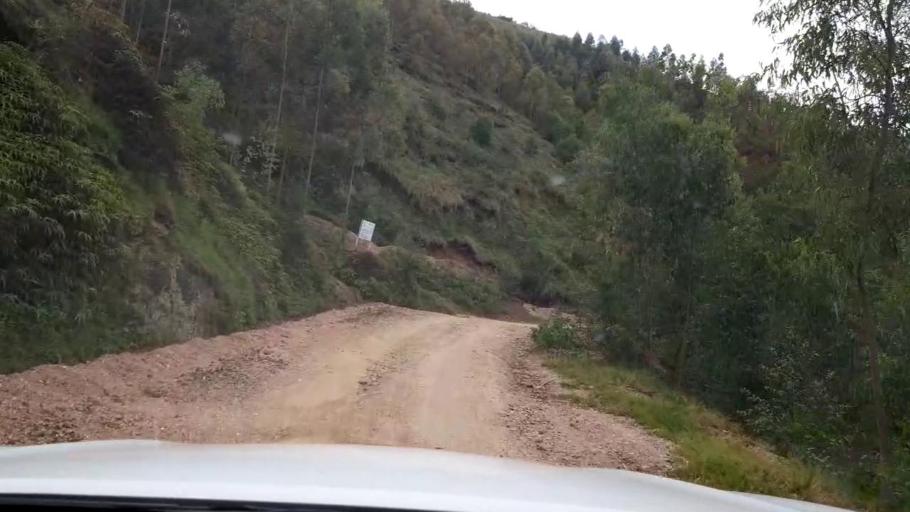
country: RW
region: Southern Province
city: Gitarama
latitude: -1.9882
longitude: 29.7082
